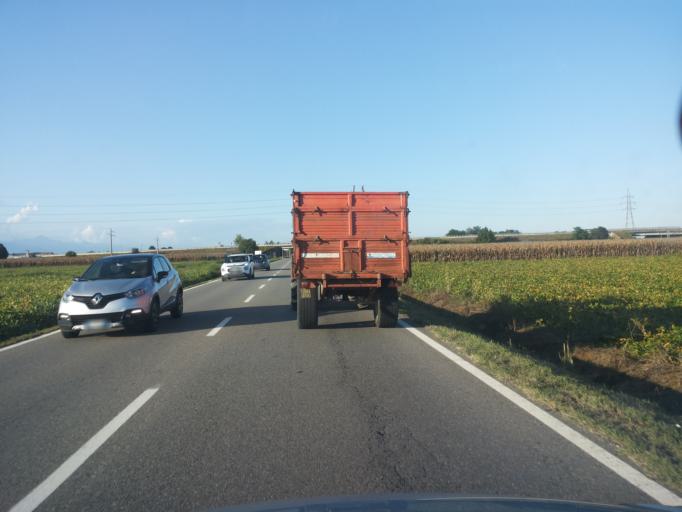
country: IT
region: Piedmont
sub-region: Provincia di Vercelli
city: Tronzano Vercellese
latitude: 45.3520
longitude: 8.1699
